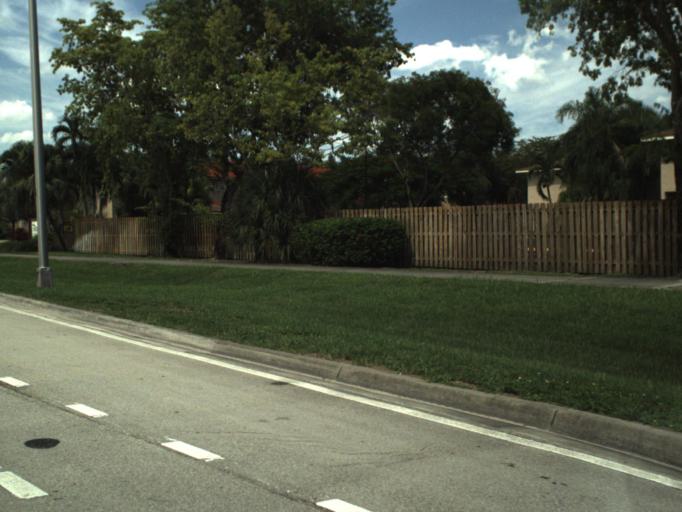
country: US
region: Florida
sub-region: Broward County
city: Davie
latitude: 26.0579
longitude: -80.2519
